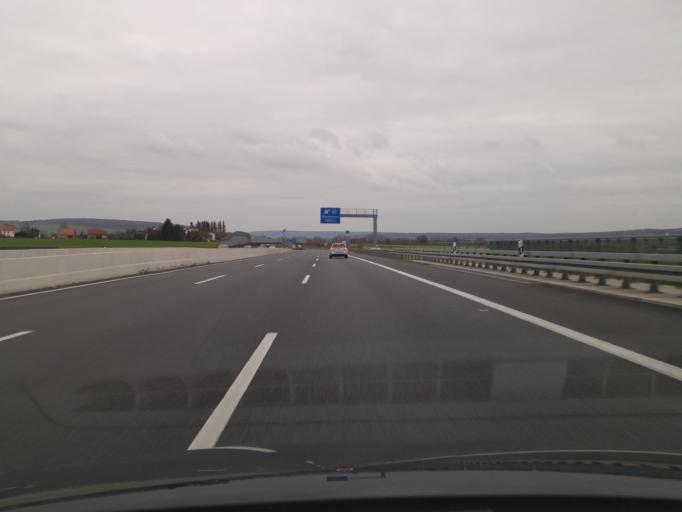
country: DE
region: Lower Saxony
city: Bockenem
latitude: 52.0102
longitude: 10.1616
